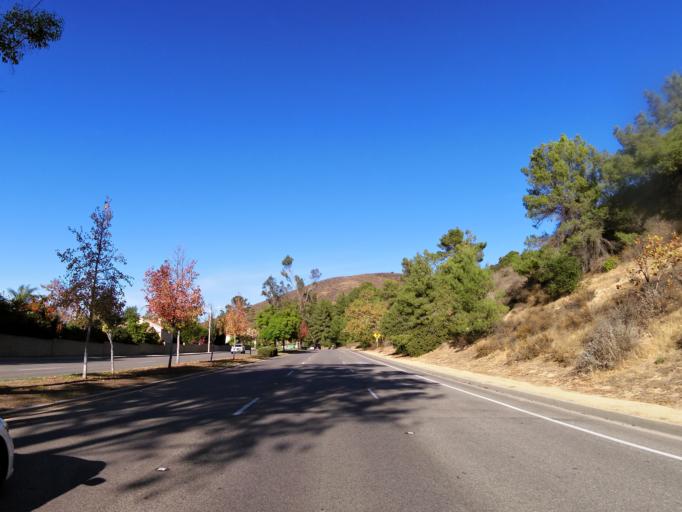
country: US
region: California
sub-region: Ventura County
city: Thousand Oaks
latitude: 34.1684
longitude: -118.8215
